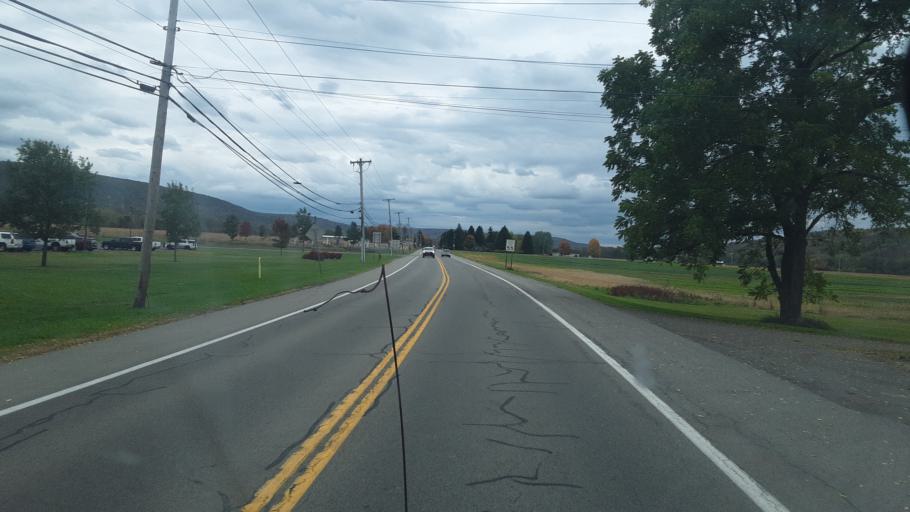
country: US
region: New York
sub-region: Allegany County
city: Belmont
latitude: 42.2124
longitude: -78.0189
